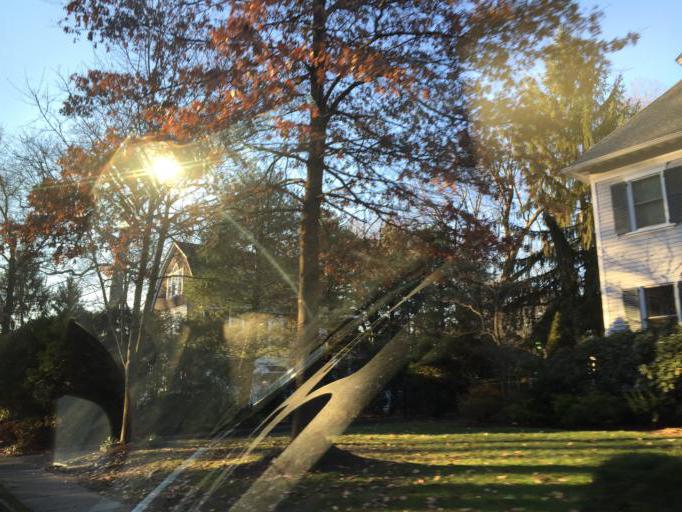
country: US
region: New Jersey
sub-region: Union County
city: Summit
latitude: 40.7135
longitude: -74.3648
